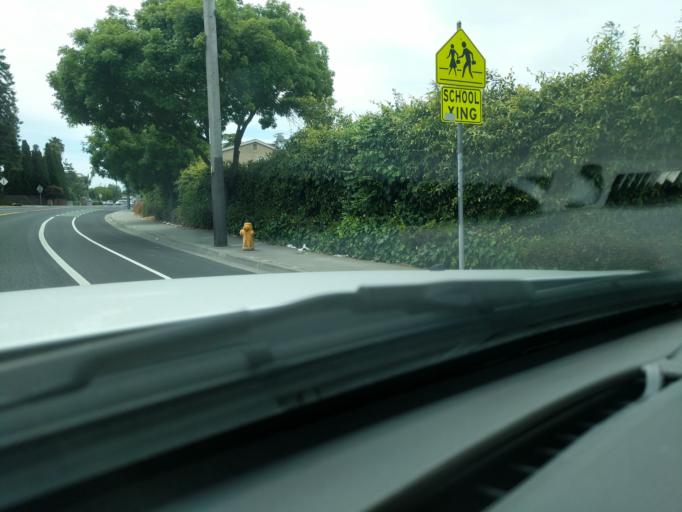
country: US
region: California
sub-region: Alameda County
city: Hayward
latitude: 37.6461
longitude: -122.0671
